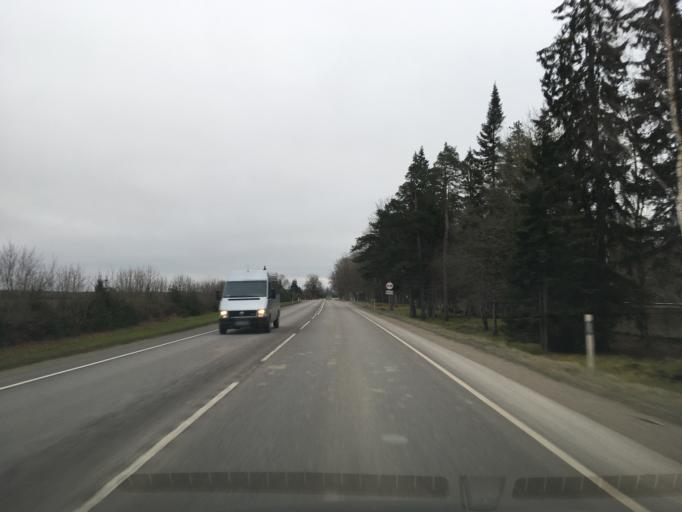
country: EE
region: Laeaene-Virumaa
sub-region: Rakvere linn
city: Rakvere
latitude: 59.3964
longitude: 26.3793
